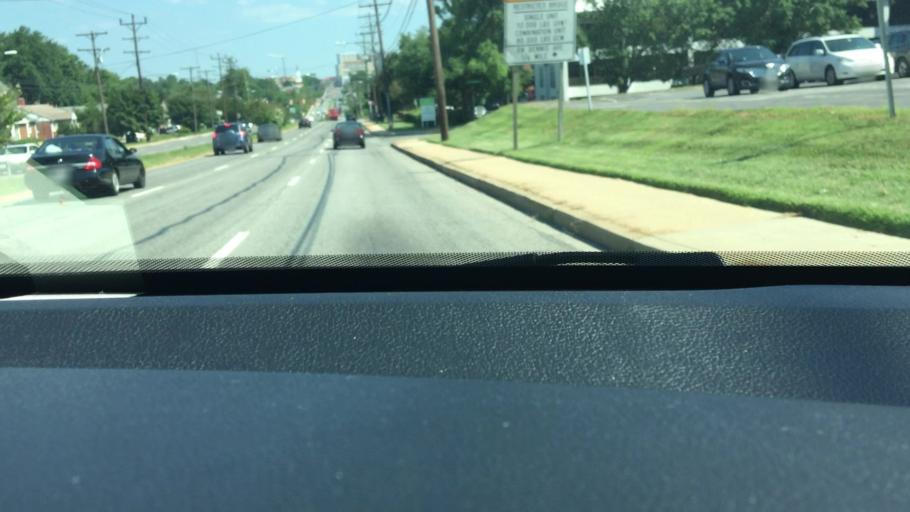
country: US
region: Maryland
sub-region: Montgomery County
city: Forest Glen
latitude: 39.0231
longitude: -77.0452
